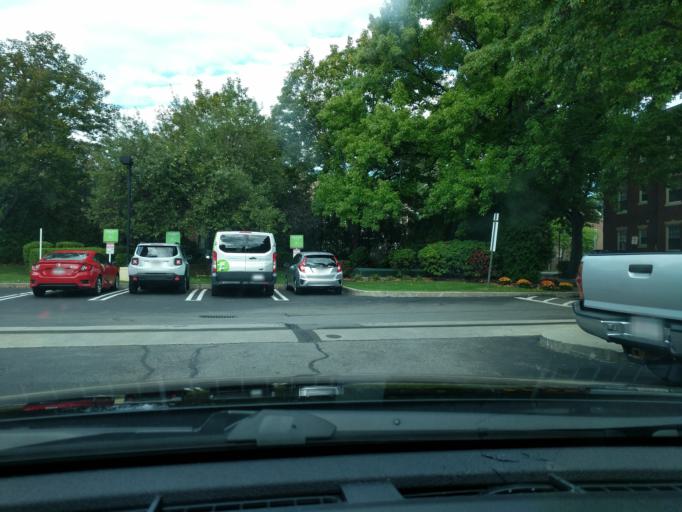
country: US
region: Massachusetts
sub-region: Norfolk County
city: Brookline
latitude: 42.3486
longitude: -71.1178
